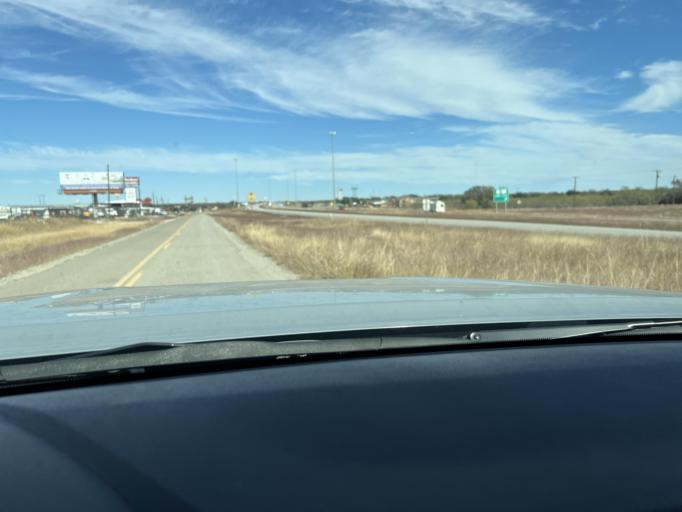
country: US
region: Texas
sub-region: Eastland County
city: Eastland
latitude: 32.3954
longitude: -98.7948
